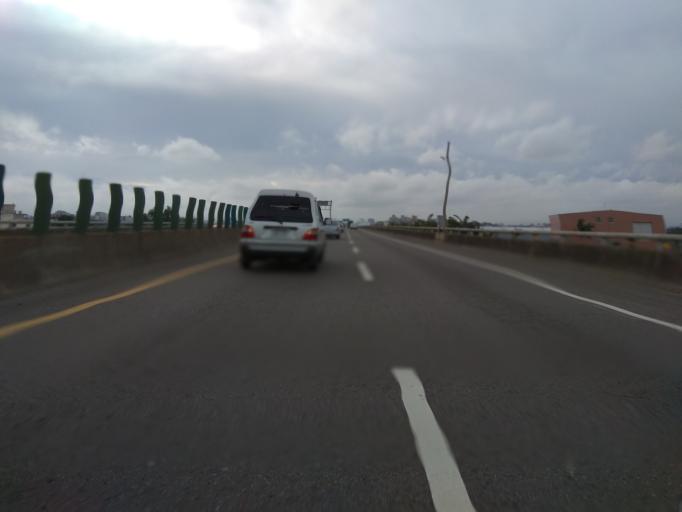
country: TW
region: Taiwan
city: Daxi
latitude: 24.9188
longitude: 121.2238
